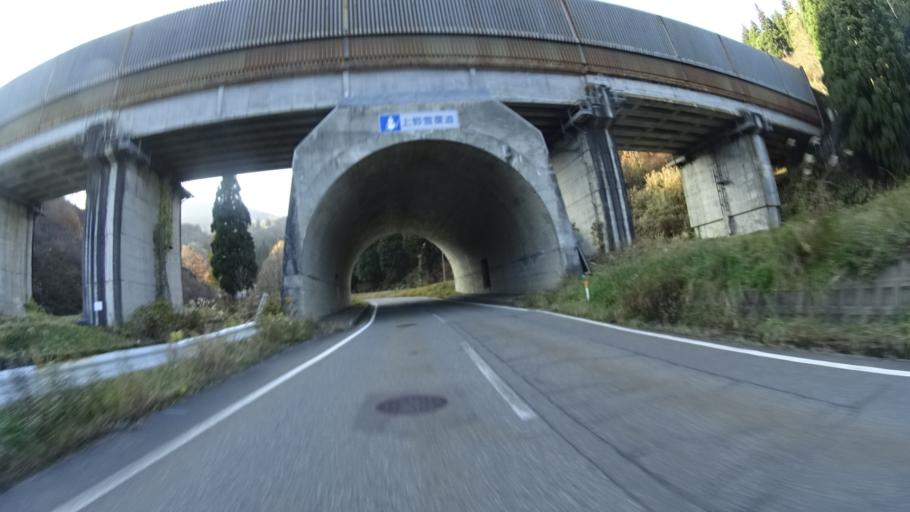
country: JP
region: Niigata
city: Shiozawa
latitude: 36.9875
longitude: 138.7916
